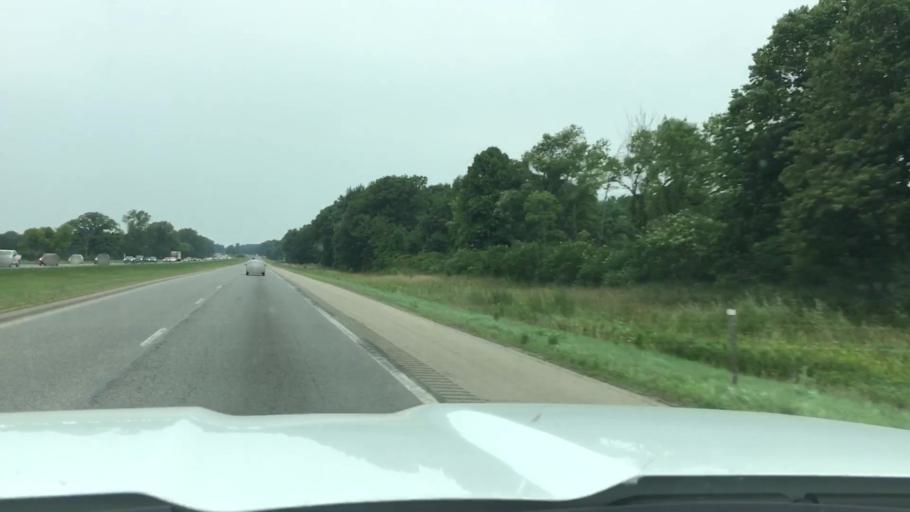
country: US
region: Michigan
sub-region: Ingham County
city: Webberville
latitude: 42.6663
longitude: -84.2290
